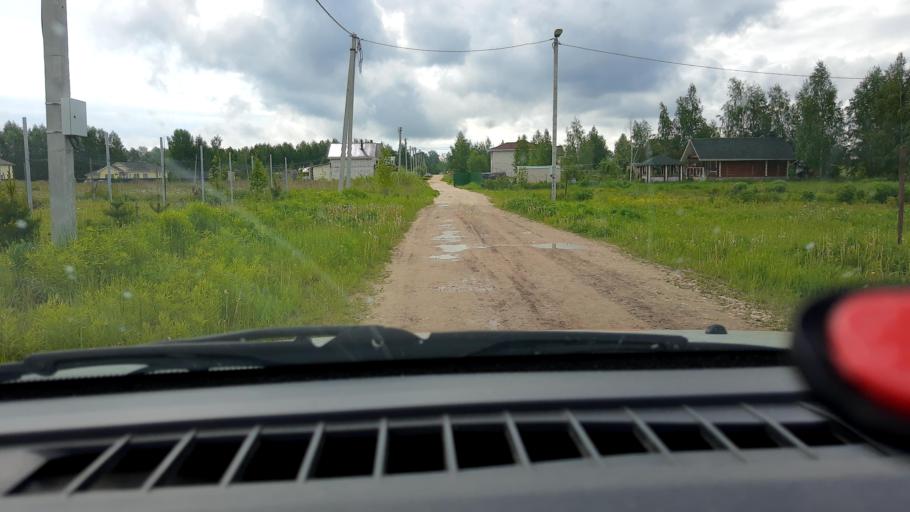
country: RU
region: Nizjnij Novgorod
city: Neklyudovo
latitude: 56.4300
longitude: 43.9729
